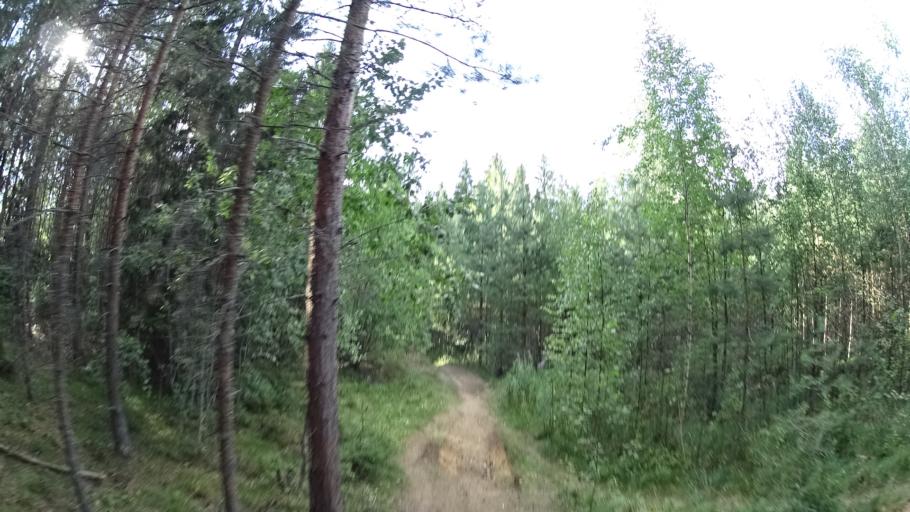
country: FI
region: Uusimaa
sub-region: Helsinki
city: Vihti
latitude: 60.3660
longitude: 24.3538
